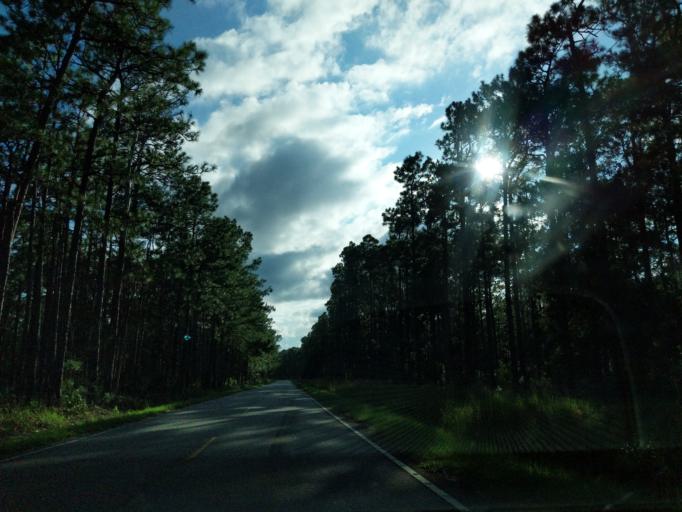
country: US
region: South Carolina
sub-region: Charleston County
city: Awendaw
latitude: 33.1354
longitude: -79.4356
